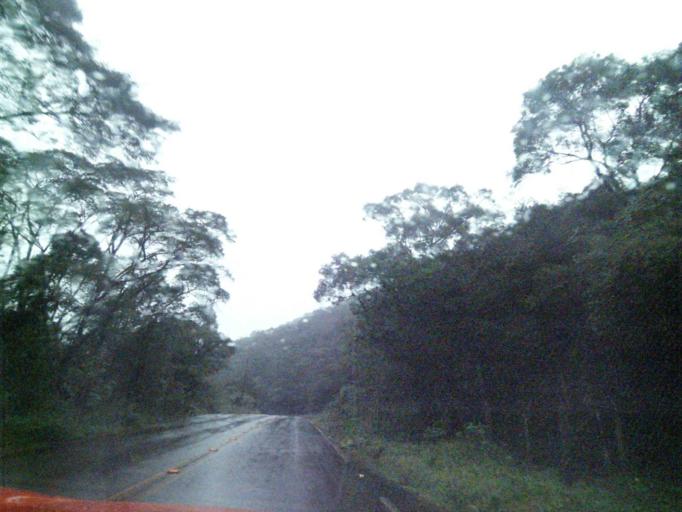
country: BR
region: Santa Catarina
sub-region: Anitapolis
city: Anitapolis
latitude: -27.7704
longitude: -49.0402
